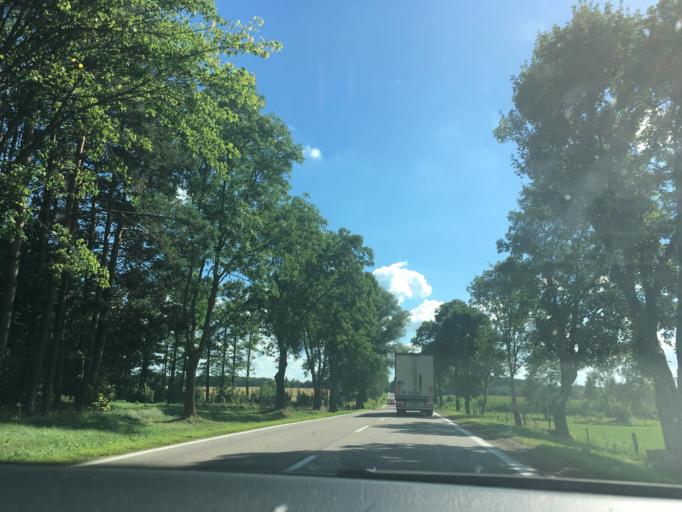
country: PL
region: Podlasie
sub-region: Powiat sokolski
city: Suchowola
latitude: 53.6116
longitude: 23.1192
